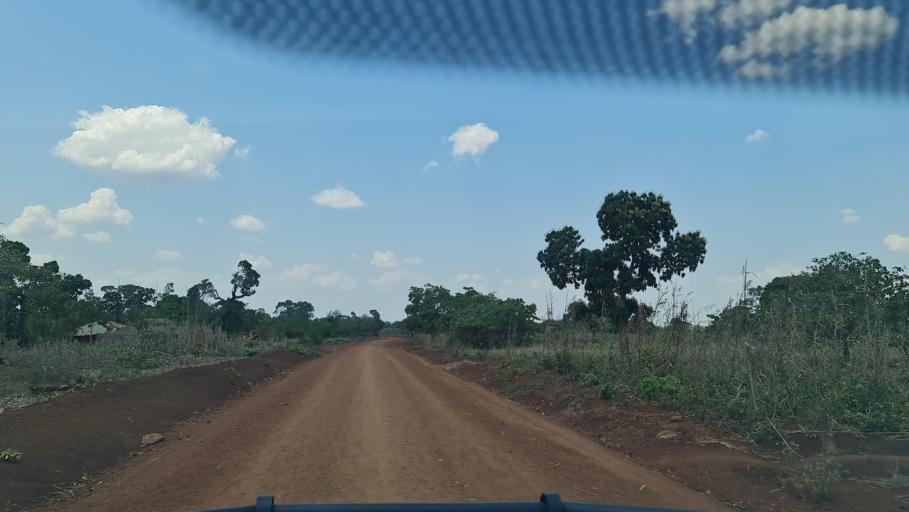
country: MZ
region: Nampula
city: Nacala
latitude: -14.8102
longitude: 40.0736
